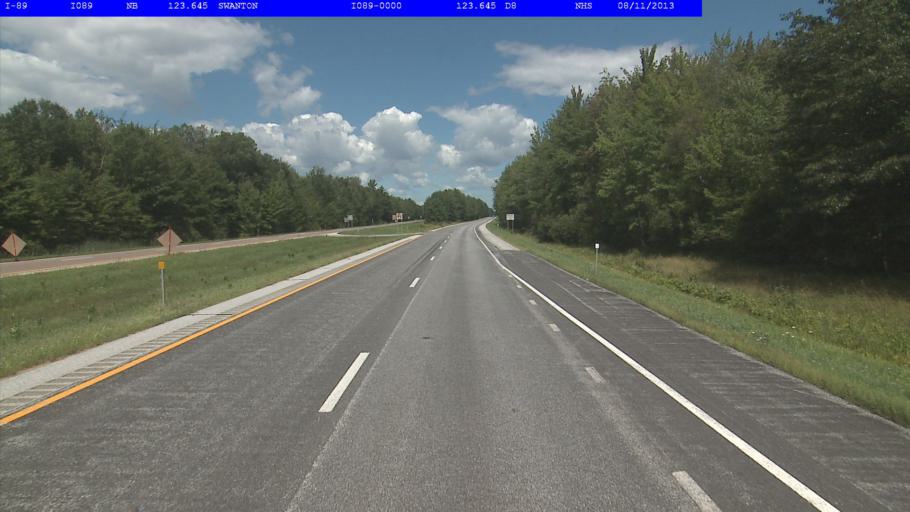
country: US
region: Vermont
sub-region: Franklin County
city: Swanton
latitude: 44.9261
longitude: -73.1093
